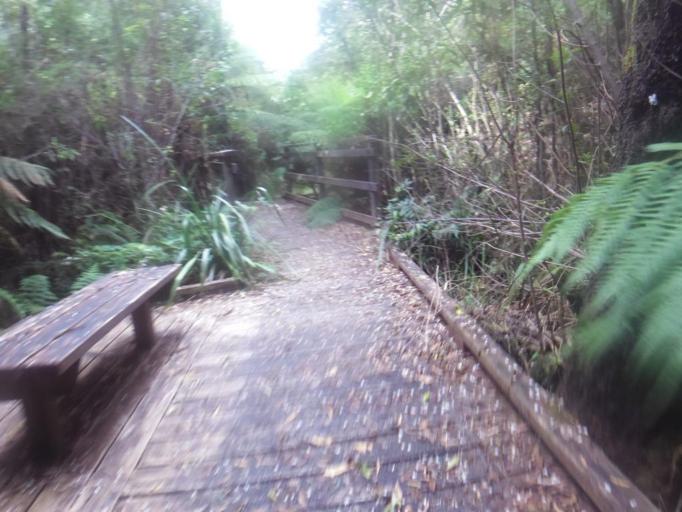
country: AU
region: Victoria
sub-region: Yarra Ranges
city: Millgrove
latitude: -37.5160
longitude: 145.7453
